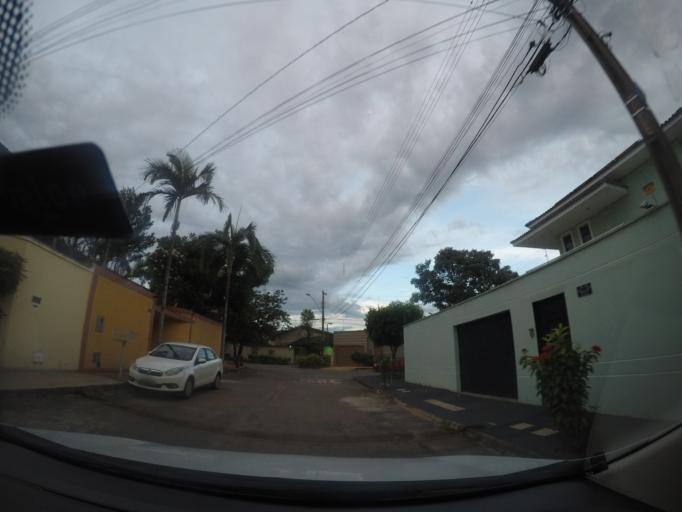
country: BR
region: Goias
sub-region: Goiania
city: Goiania
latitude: -16.6491
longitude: -49.2257
